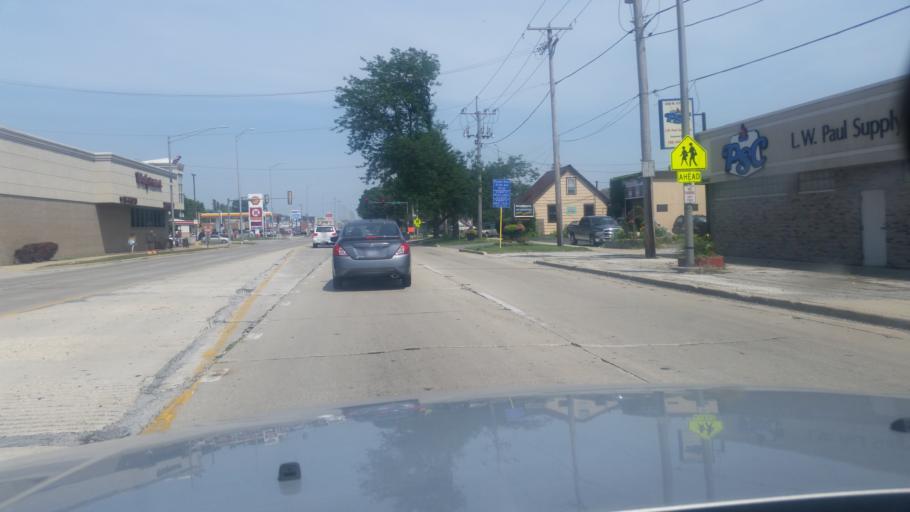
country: US
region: Illinois
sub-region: Cook County
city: Chicago Ridge
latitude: 41.6903
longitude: -87.7805
